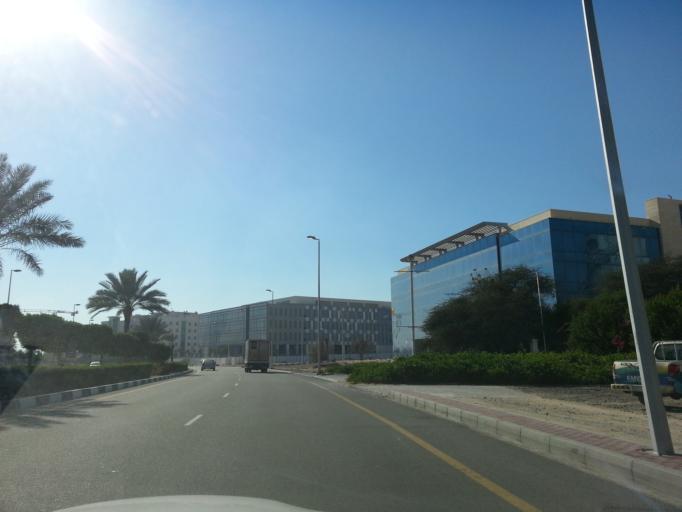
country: AE
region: Dubai
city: Dubai
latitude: 25.0093
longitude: 55.1598
